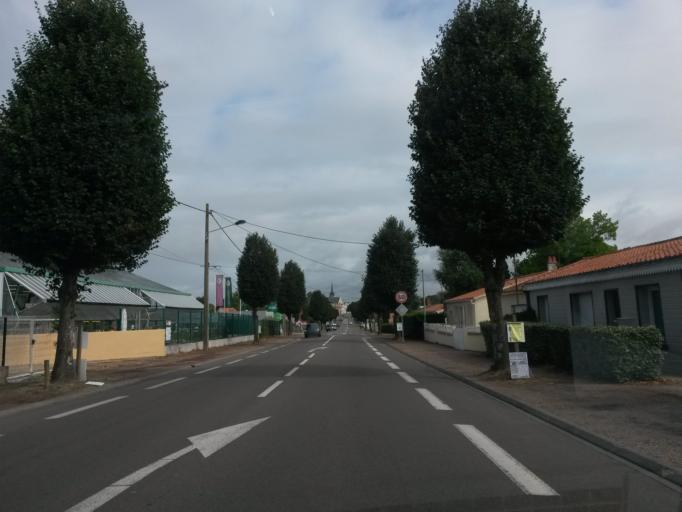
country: FR
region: Pays de la Loire
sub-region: Departement de la Vendee
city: Olonne-sur-Mer
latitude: 46.5291
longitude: -1.7743
